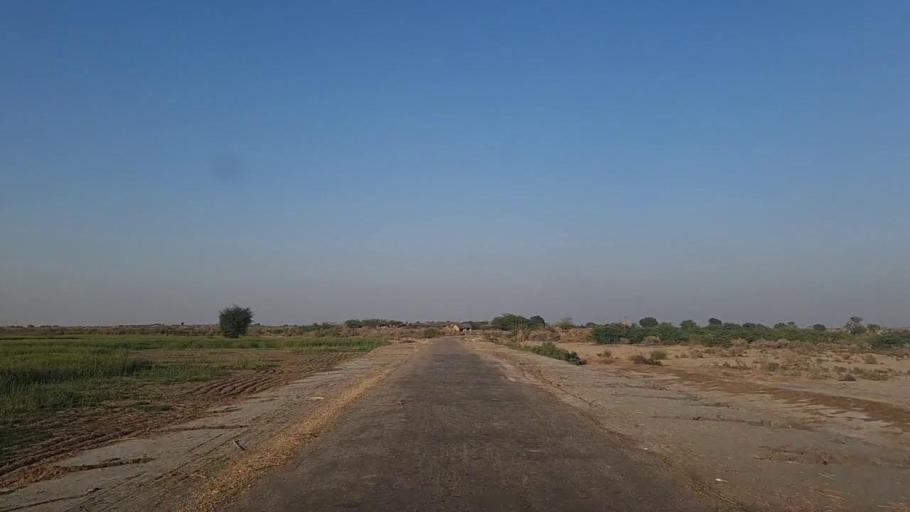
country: PK
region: Sindh
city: Jam Sahib
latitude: 26.3387
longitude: 68.6686
